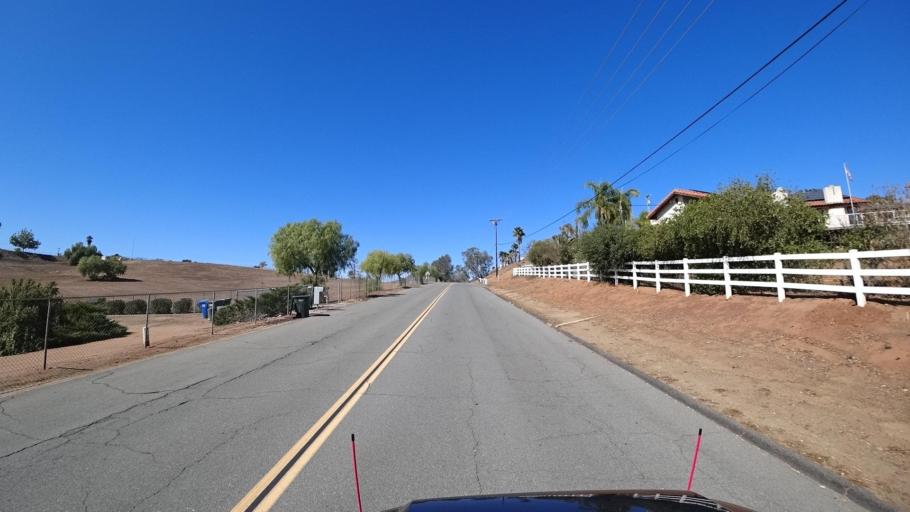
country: US
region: California
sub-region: San Diego County
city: Harbison Canyon
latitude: 32.8661
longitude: -116.8539
